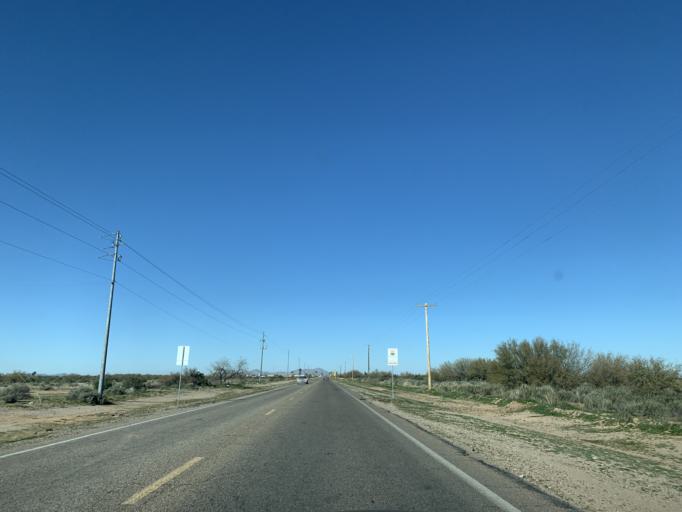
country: US
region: Arizona
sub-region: Pinal County
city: Arizona City
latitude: 32.7918
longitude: -111.6710
